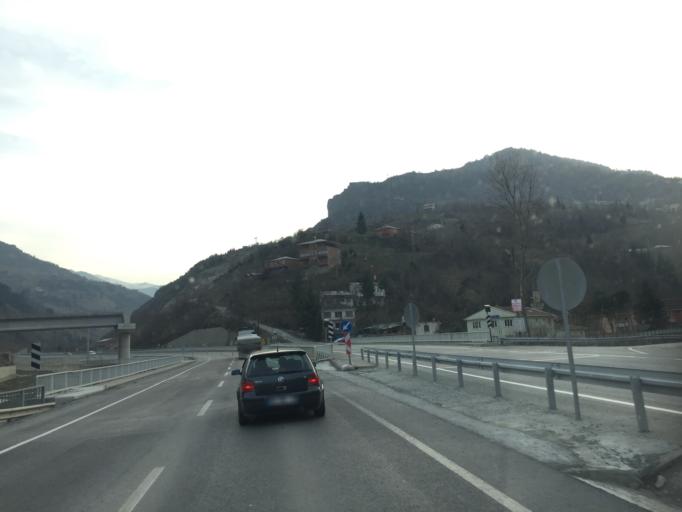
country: TR
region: Trabzon
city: Macka
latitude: 40.8009
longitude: 39.5855
